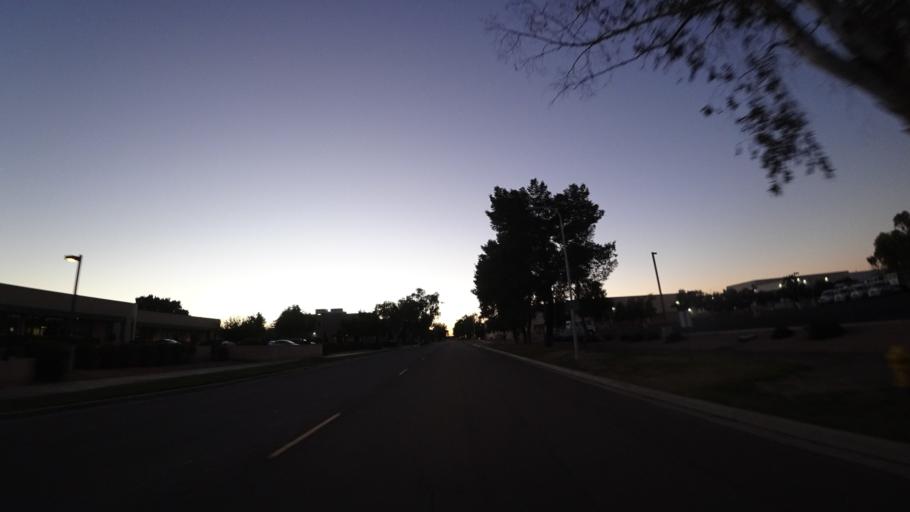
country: US
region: Arizona
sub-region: Maricopa County
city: Tempe Junction
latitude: 33.4136
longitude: -111.9708
